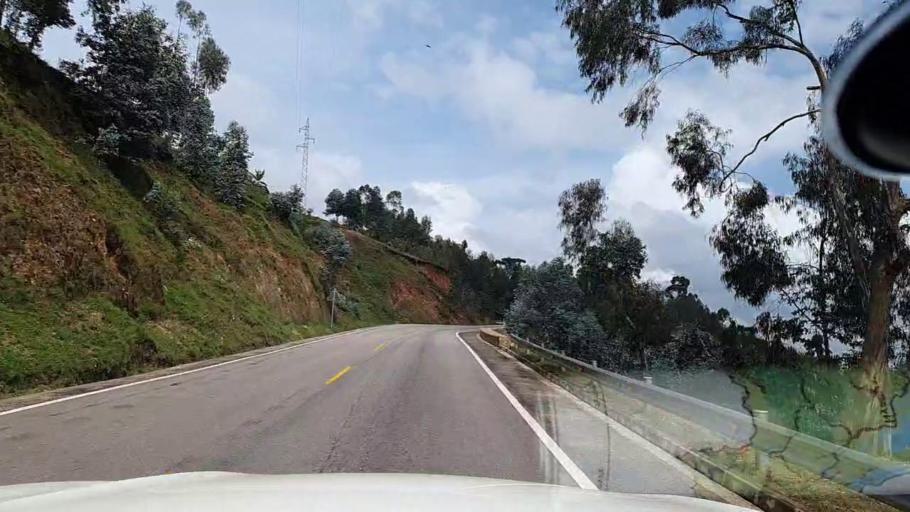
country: RW
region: Southern Province
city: Nzega
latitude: -2.5067
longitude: 29.4990
